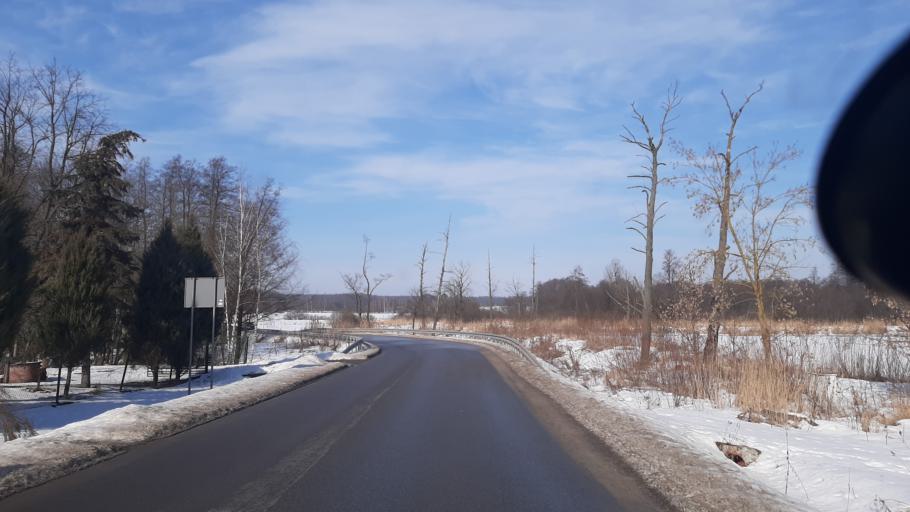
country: PL
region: Lublin Voivodeship
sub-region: Powiat pulawski
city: Kurow
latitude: 51.4106
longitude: 22.2064
